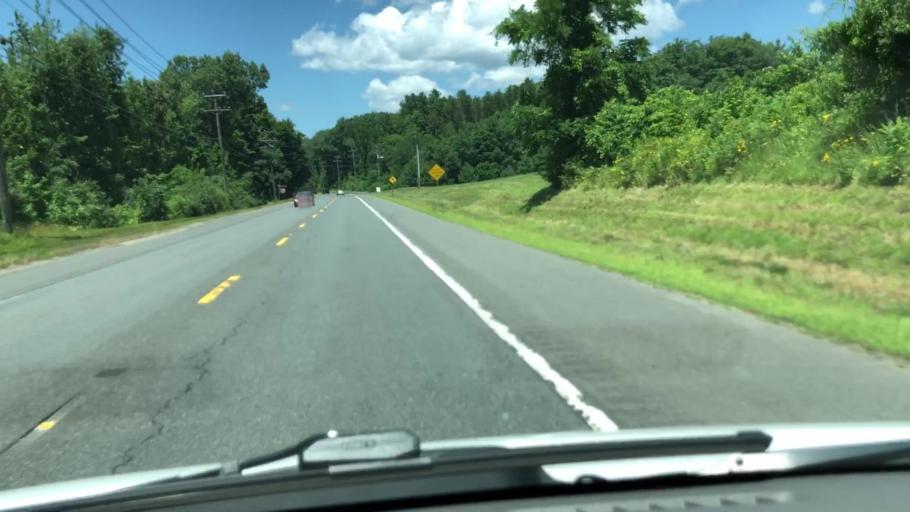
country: US
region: Massachusetts
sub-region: Hampshire County
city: North Amherst
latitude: 42.4359
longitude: -72.5465
